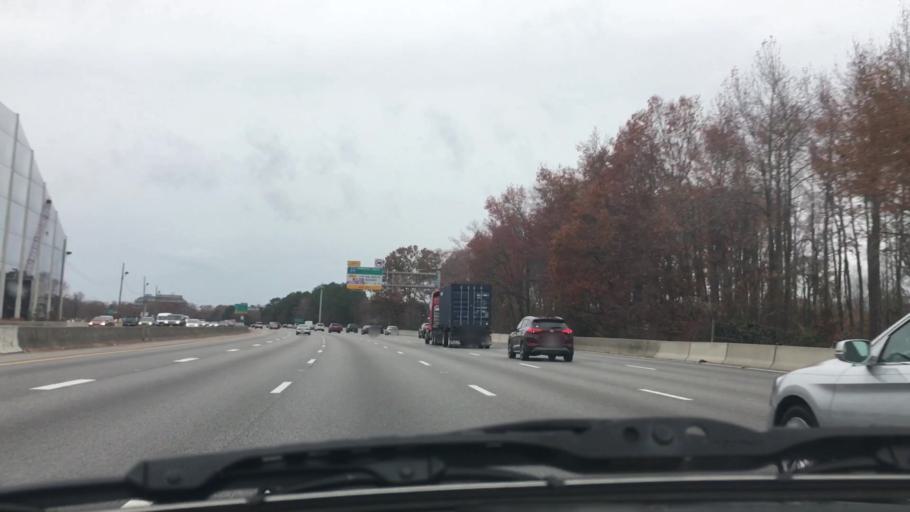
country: US
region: Virginia
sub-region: City of Chesapeake
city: Chesapeake
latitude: 36.8431
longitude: -76.1666
